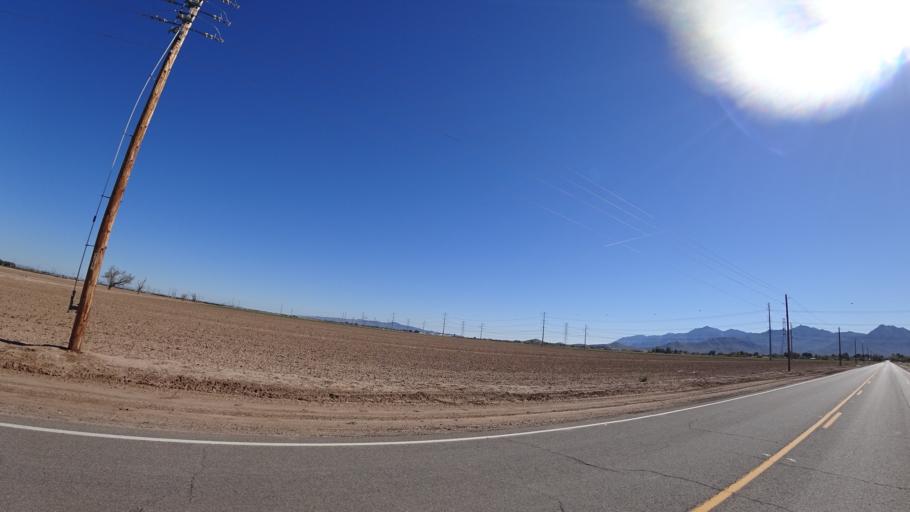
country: US
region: Arizona
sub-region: Maricopa County
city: Avondale
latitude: 33.4054
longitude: -112.3405
